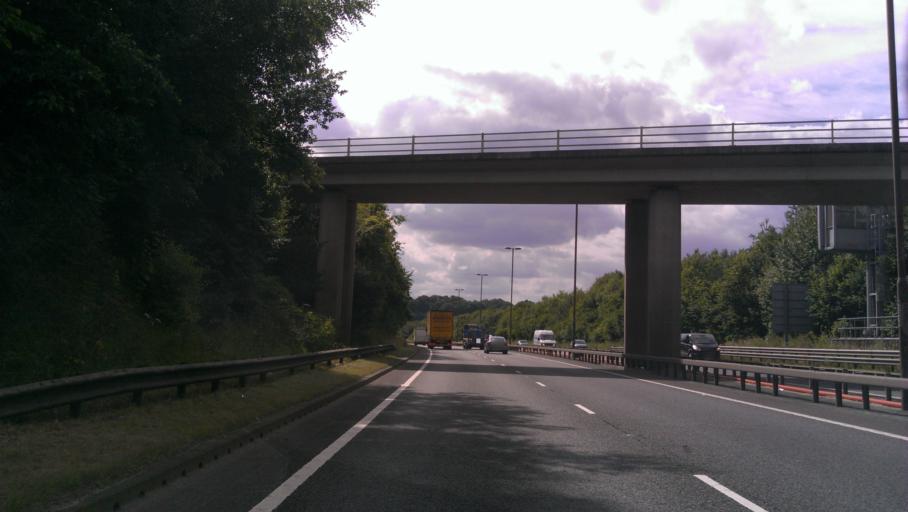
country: GB
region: England
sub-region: Kent
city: Strood
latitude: 51.4112
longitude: 0.4814
